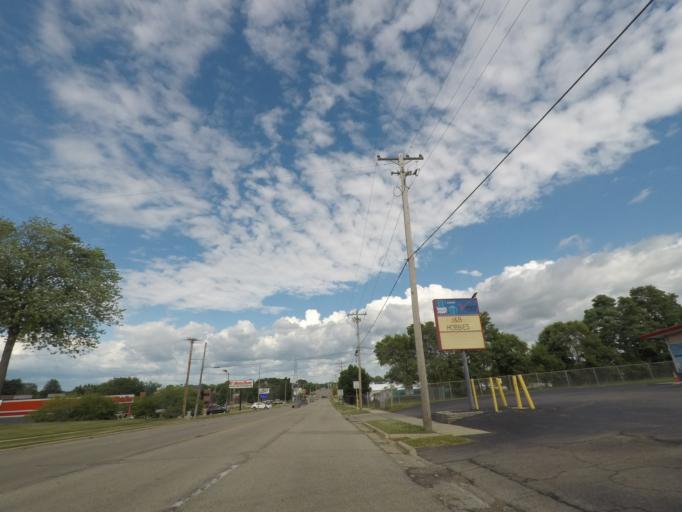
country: US
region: Wisconsin
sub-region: Rock County
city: Janesville
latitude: 42.6791
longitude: -89.0560
